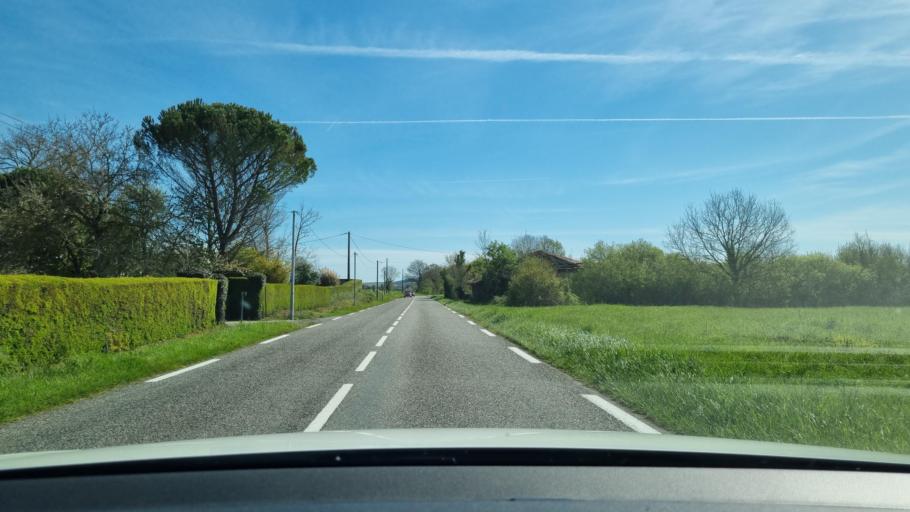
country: FR
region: Midi-Pyrenees
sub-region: Departement du Gers
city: Lombez
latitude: 43.4242
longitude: 0.8193
